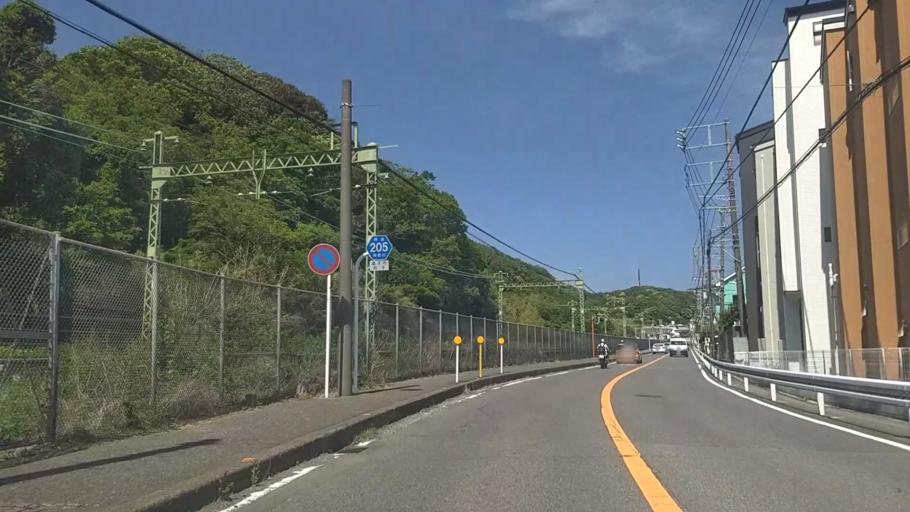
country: JP
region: Kanagawa
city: Zushi
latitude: 35.3080
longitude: 139.5956
